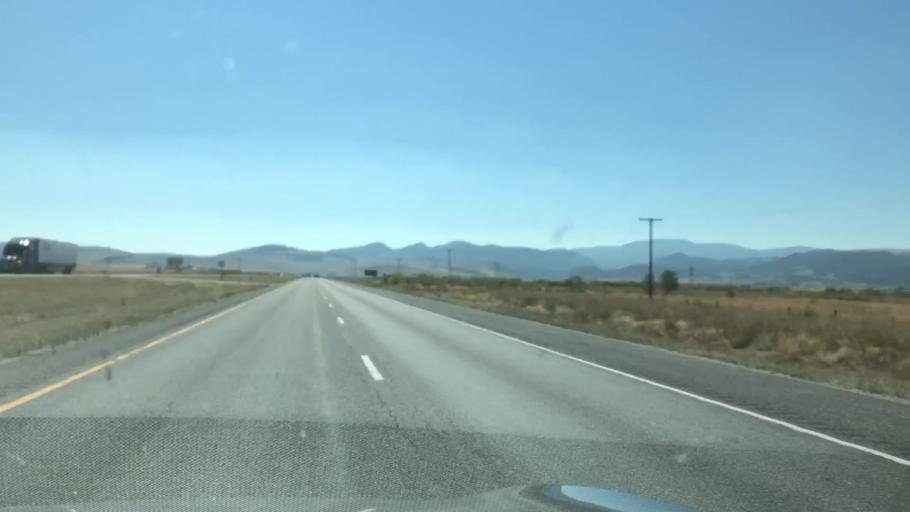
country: US
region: Montana
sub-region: Deer Lodge County
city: Warm Springs
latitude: 46.0865
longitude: -112.7892
